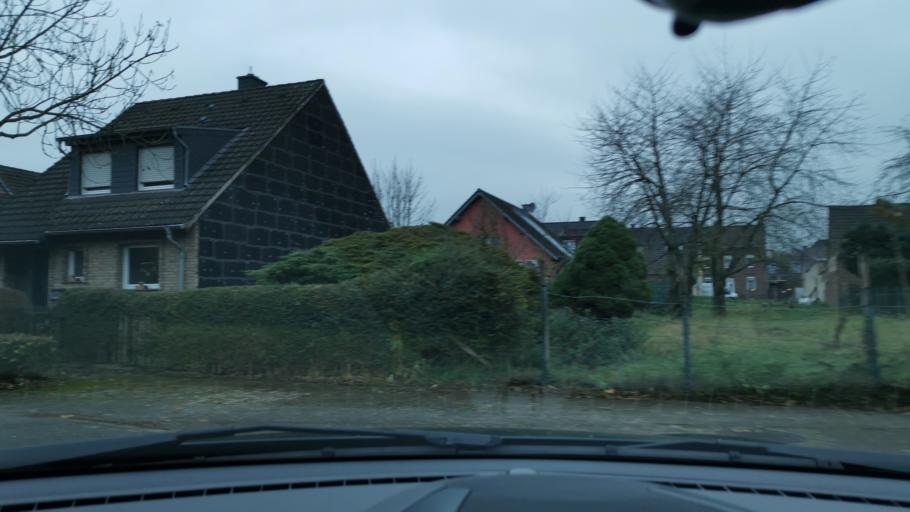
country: DE
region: North Rhine-Westphalia
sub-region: Regierungsbezirk Dusseldorf
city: Neubrueck
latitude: 51.1274
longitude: 6.6261
